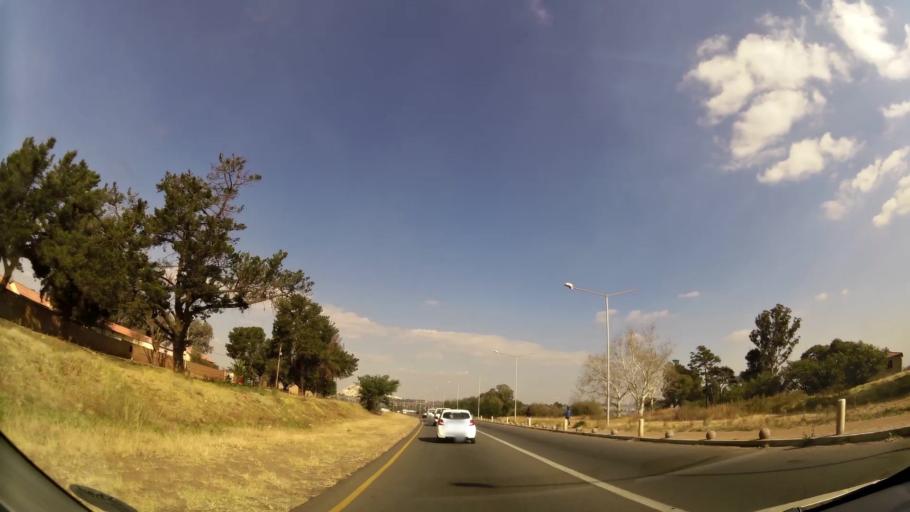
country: ZA
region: Gauteng
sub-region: West Rand District Municipality
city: Krugersdorp
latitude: -26.0841
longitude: 27.7596
